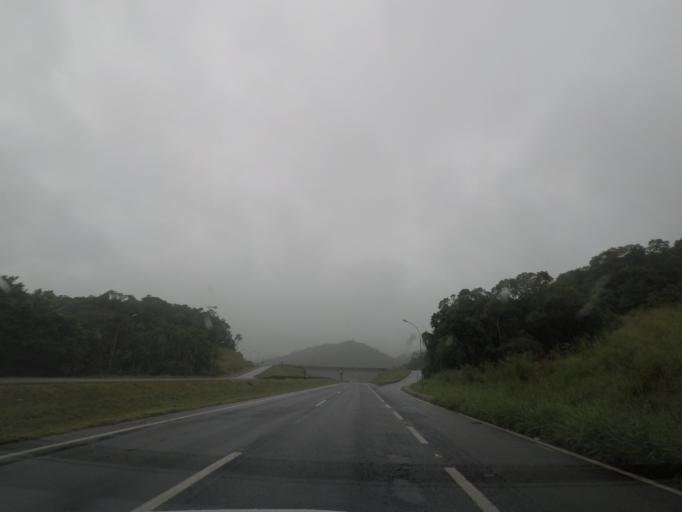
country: BR
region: Sao Paulo
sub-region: Juquia
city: Juquia
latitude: -24.3550
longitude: -47.6705
